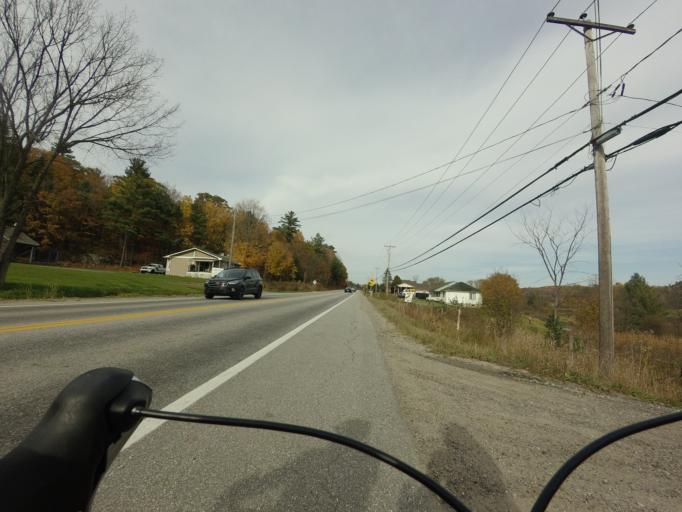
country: CA
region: Quebec
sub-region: Outaouais
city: Val-des-Monts
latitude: 45.5774
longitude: -75.6193
